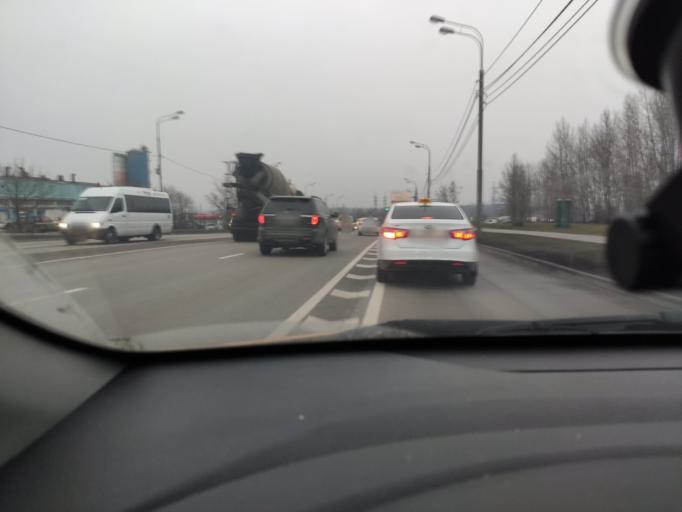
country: RU
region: Moskovskaya
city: Biryulevo Zapadnoye
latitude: 55.6002
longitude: 37.6371
